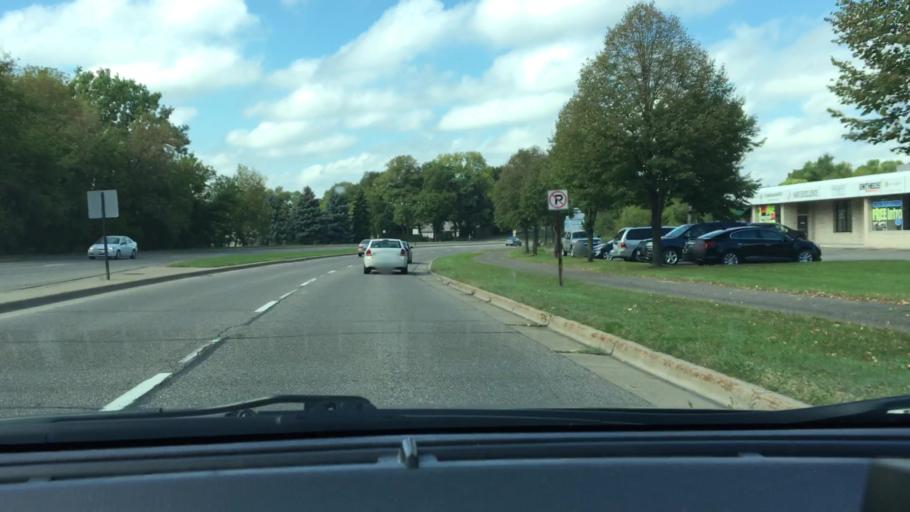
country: US
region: Minnesota
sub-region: Hennepin County
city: Maple Grove
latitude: 45.0586
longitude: -93.4265
